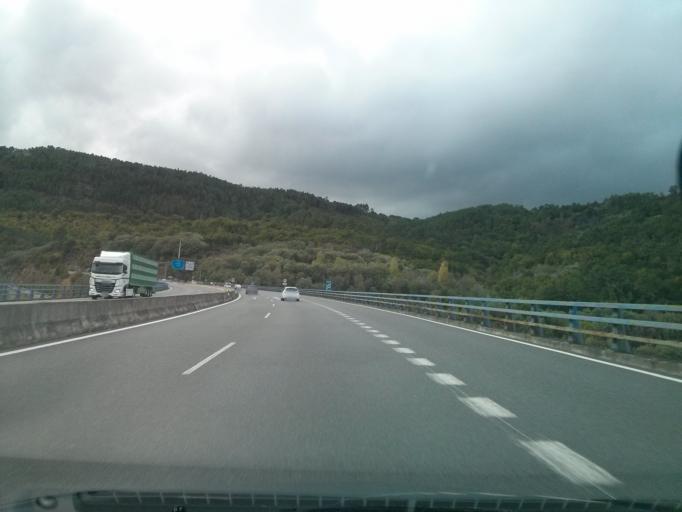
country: ES
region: Galicia
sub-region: Provincia de Ourense
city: Punxin
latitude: 42.3435
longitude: -8.0055
